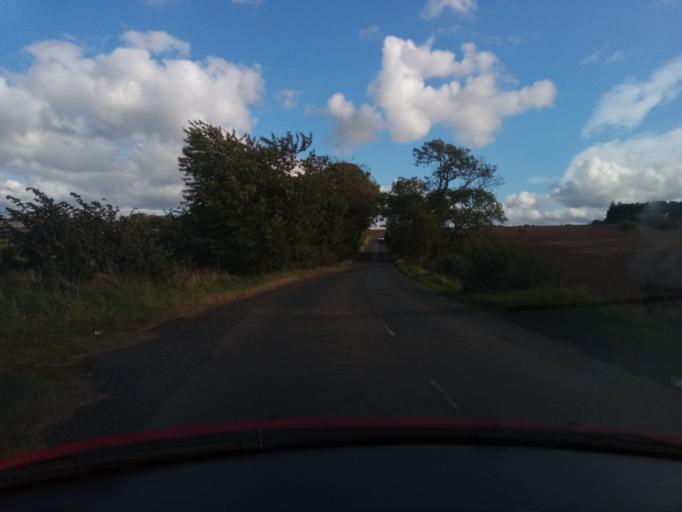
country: GB
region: Scotland
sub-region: The Scottish Borders
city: Kelso
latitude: 55.5710
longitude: -2.3716
